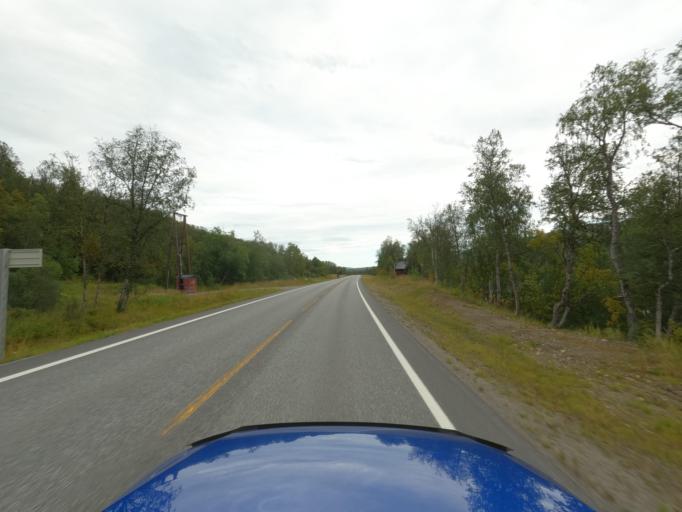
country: NO
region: Finnmark Fylke
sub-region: Kvalsund
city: Kvalsund
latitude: 70.4466
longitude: 24.4059
